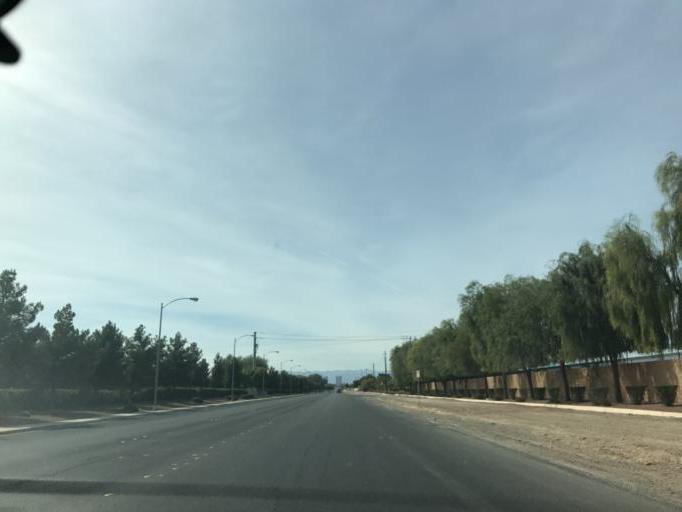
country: US
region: Nevada
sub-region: Clark County
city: Whitney
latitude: 36.1297
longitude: -115.0408
